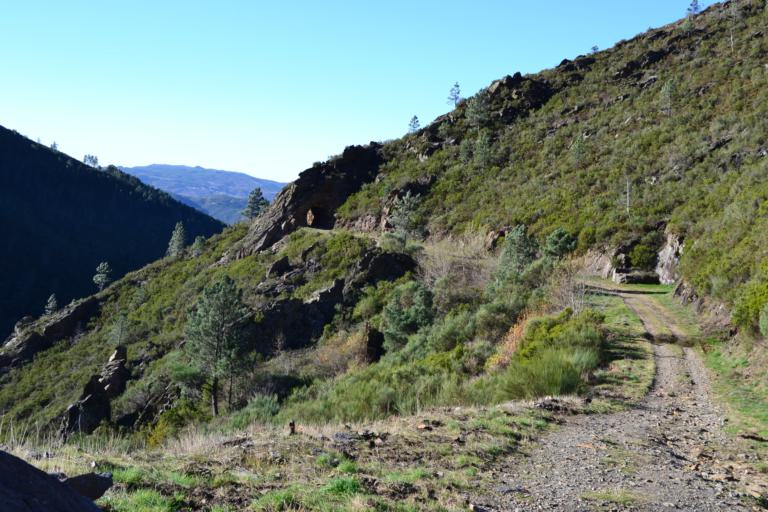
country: PT
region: Vila Real
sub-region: Mesao Frio
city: Mesao Frio
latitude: 41.2643
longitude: -7.9192
